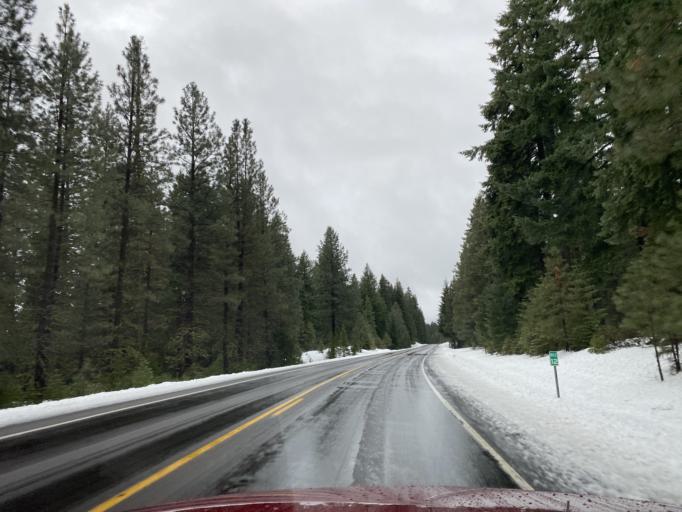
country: US
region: Oregon
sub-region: Klamath County
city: Klamath Falls
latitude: 42.5031
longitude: -122.0828
